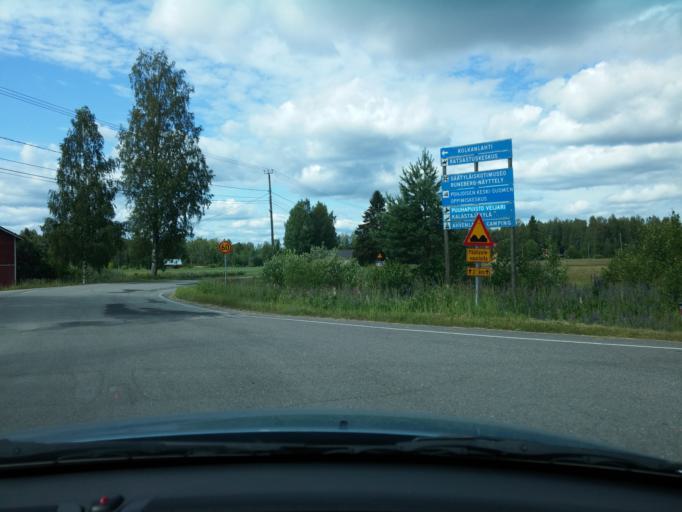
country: FI
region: Central Finland
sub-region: Saarijaervi-Viitasaari
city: Saarijaervi
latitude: 62.7345
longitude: 25.1875
